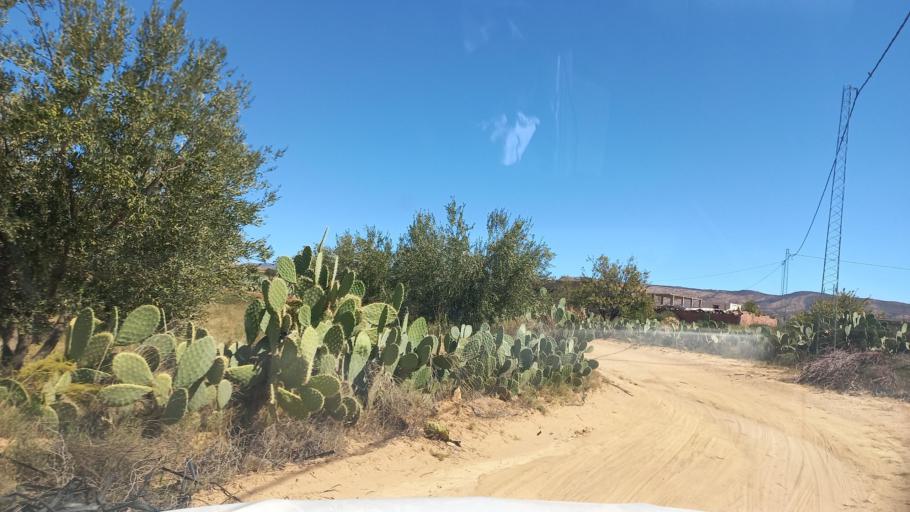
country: TN
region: Al Qasrayn
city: Sbiba
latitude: 35.3467
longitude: 9.0978
